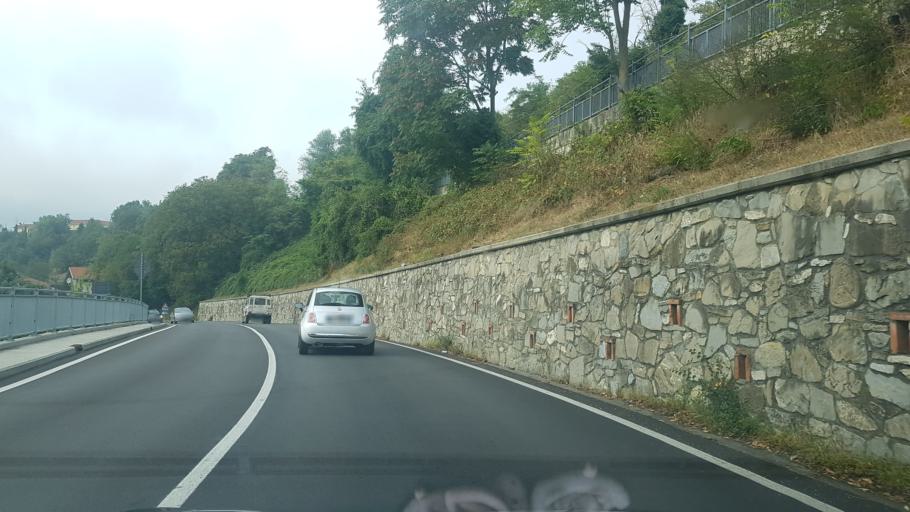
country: IT
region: Piedmont
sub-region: Provincia di Cuneo
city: Ceva
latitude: 44.3853
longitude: 8.0269
